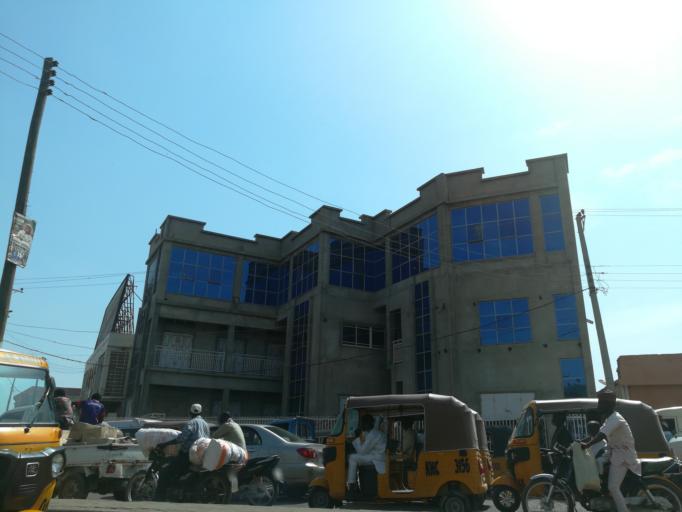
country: NG
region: Kano
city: Kano
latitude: 12.0150
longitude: 8.5186
